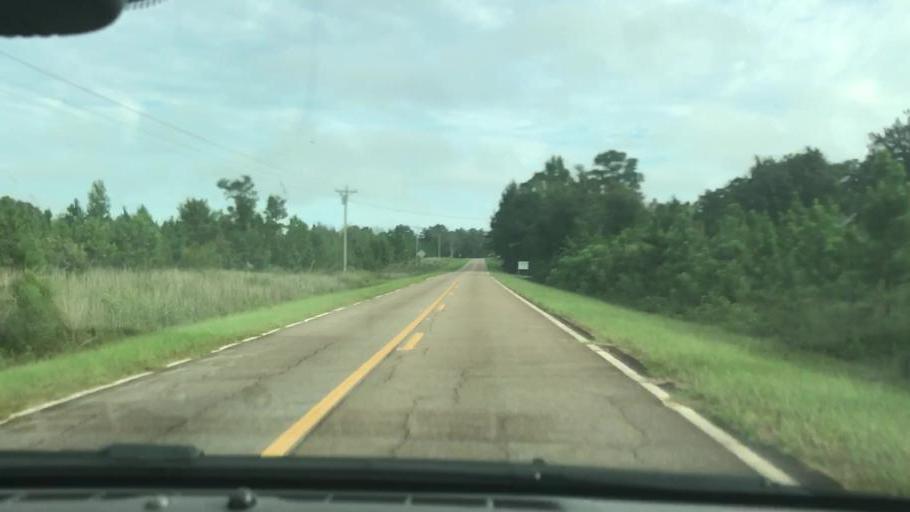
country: US
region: Georgia
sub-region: Stewart County
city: Lumpkin
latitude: 32.0633
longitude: -84.9027
